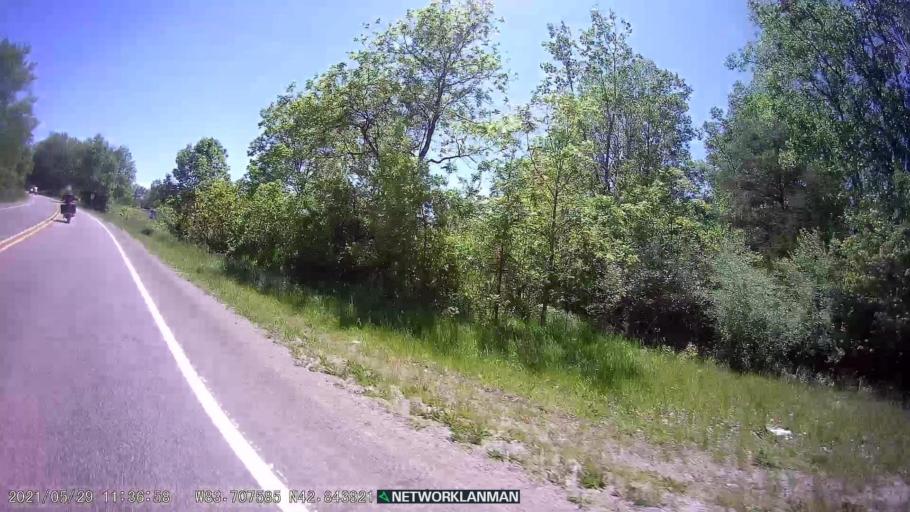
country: US
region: Michigan
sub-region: Genesee County
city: Lake Fenton
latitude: 42.8436
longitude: -83.7076
